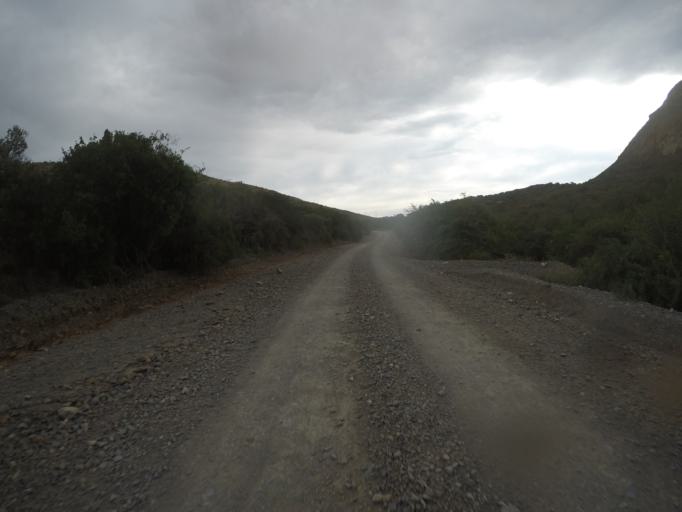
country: ZA
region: Eastern Cape
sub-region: Cacadu District Municipality
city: Willowmore
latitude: -33.5136
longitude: 23.8178
